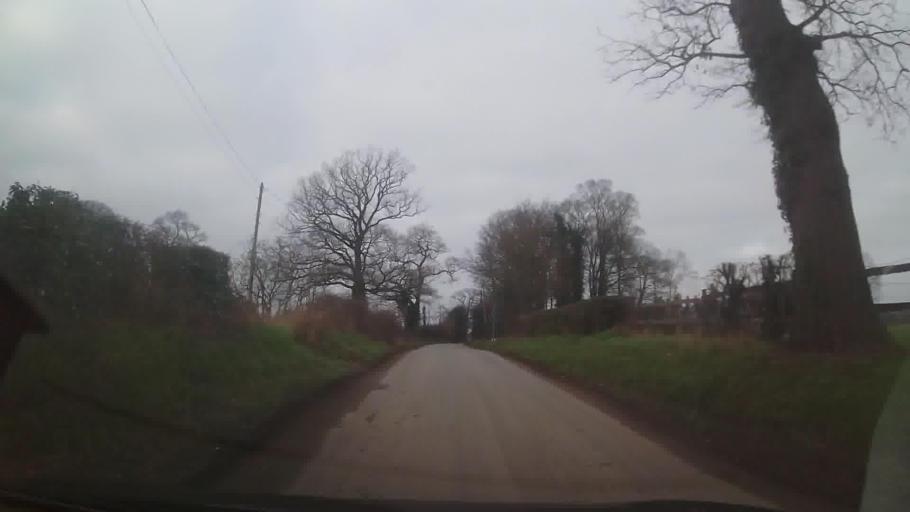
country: GB
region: England
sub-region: Shropshire
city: Bicton
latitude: 52.7601
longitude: -2.8407
